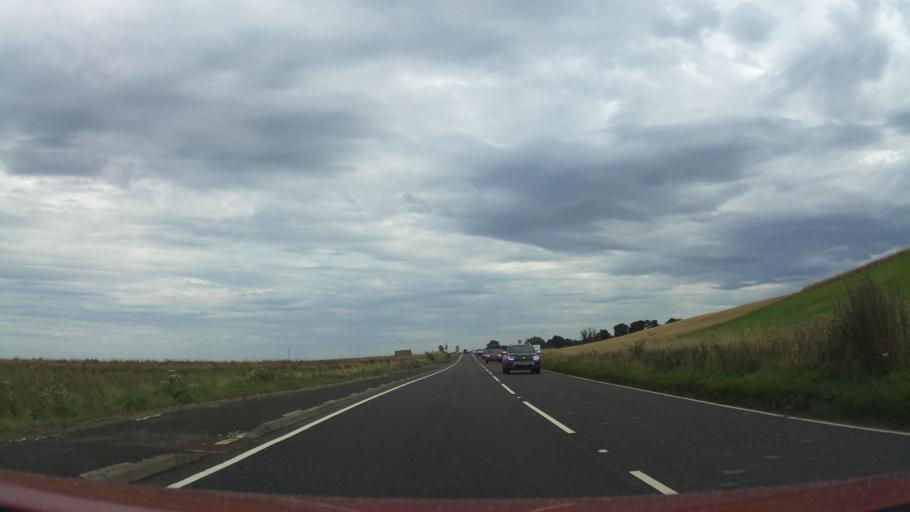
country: GB
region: Scotland
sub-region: Fife
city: Strathkinness
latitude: 56.3589
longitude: -2.8675
